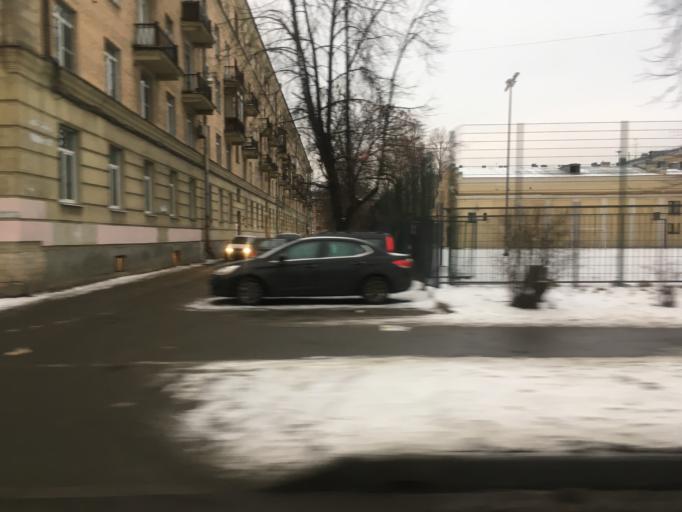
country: RU
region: St.-Petersburg
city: Obukhovo
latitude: 59.8779
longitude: 30.4392
